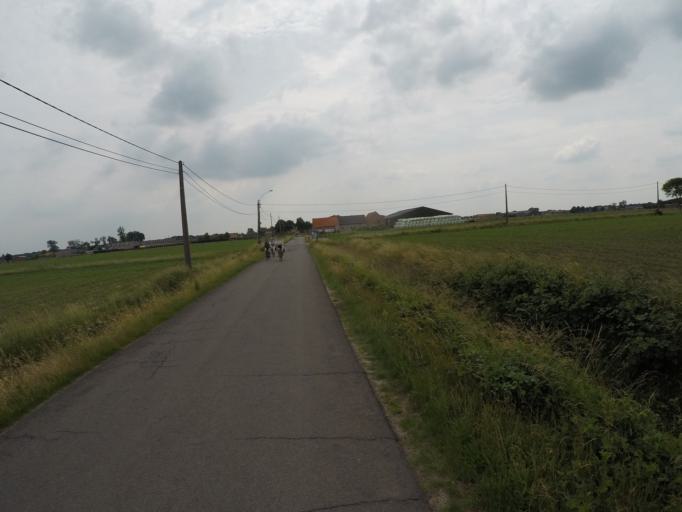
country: BE
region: Flanders
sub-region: Provincie Antwerpen
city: Wuustwezel
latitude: 51.4065
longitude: 4.5904
